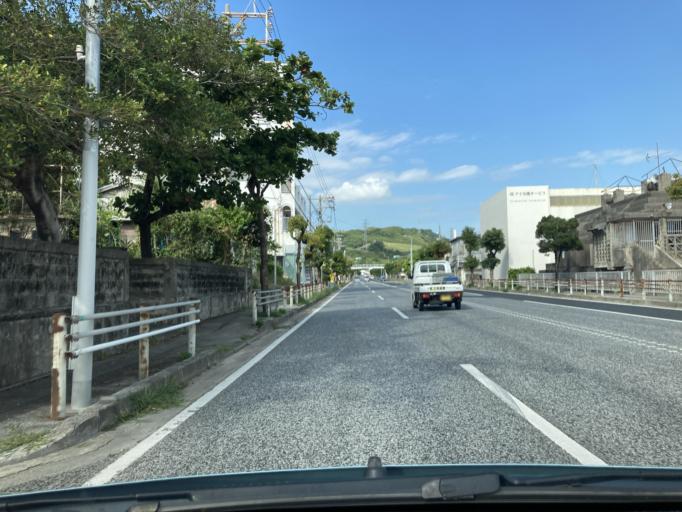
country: JP
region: Okinawa
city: Ginowan
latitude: 26.2663
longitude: 127.7903
